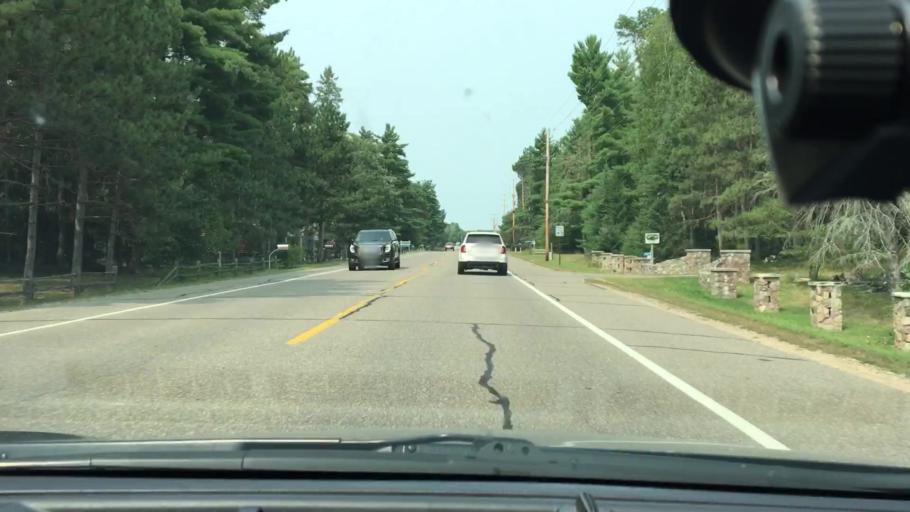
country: US
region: Minnesota
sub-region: Crow Wing County
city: Cross Lake
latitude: 46.5886
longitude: -94.1315
